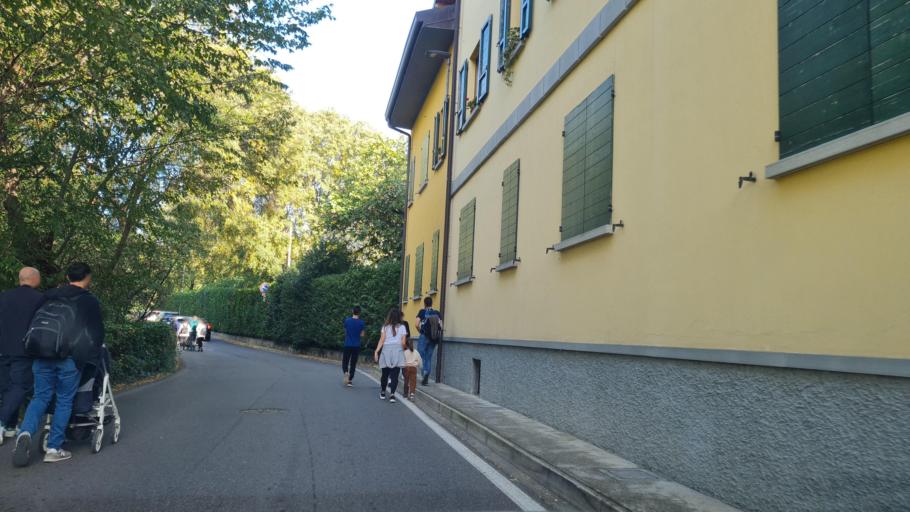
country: IT
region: Lombardy
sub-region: Provincia di Bergamo
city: Ponte San Pietro
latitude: 45.7148
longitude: 9.5964
